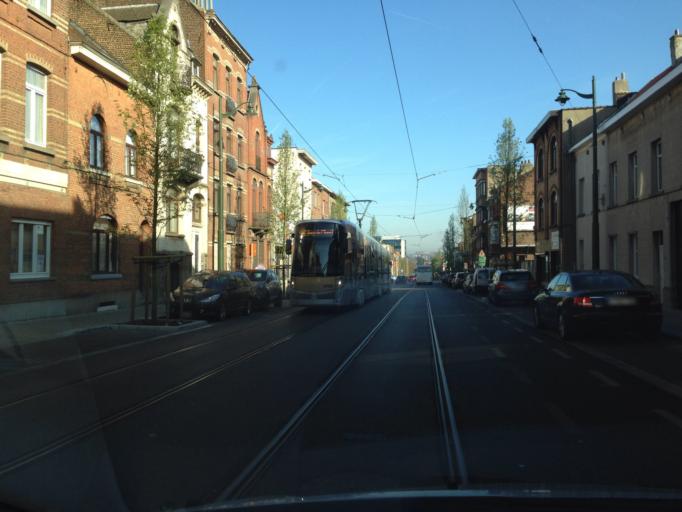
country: BE
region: Flanders
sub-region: Provincie Vlaams-Brabant
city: Dilbeek
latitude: 50.8682
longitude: 4.2933
